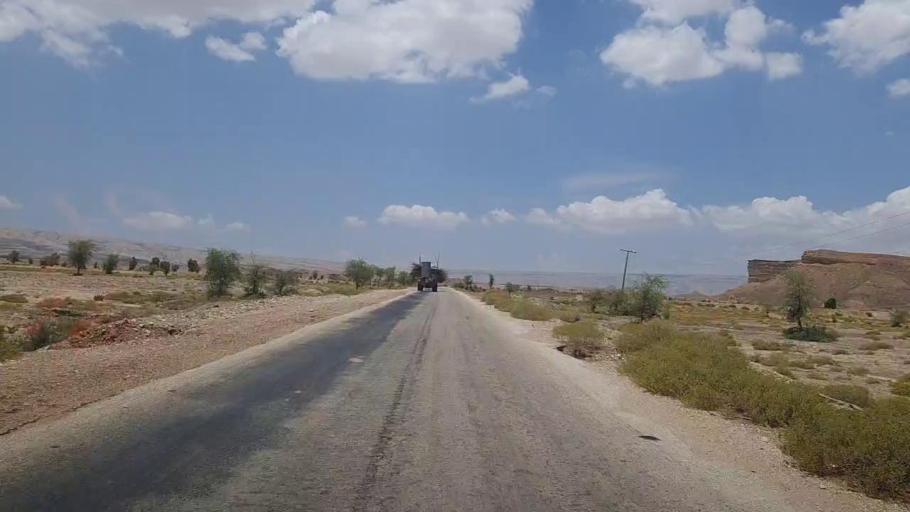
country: PK
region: Sindh
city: Sehwan
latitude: 26.3168
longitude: 67.6436
